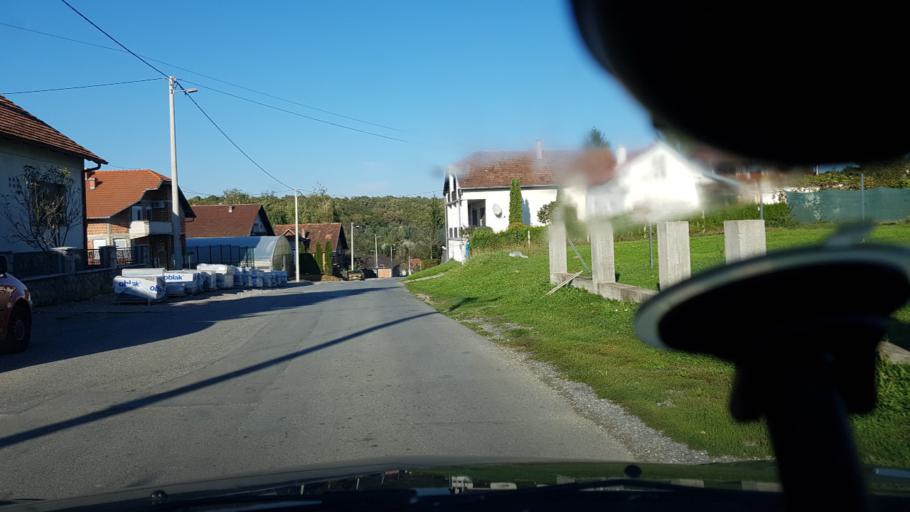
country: HR
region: Bjelovarsko-Bilogorska
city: Bjelovar
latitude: 45.9218
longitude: 16.8628
